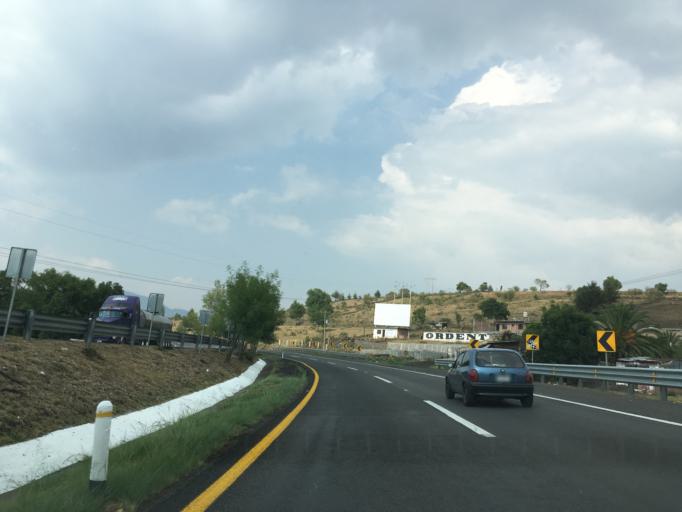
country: MX
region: Michoacan
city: Huiramba
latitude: 19.5496
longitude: -101.4327
